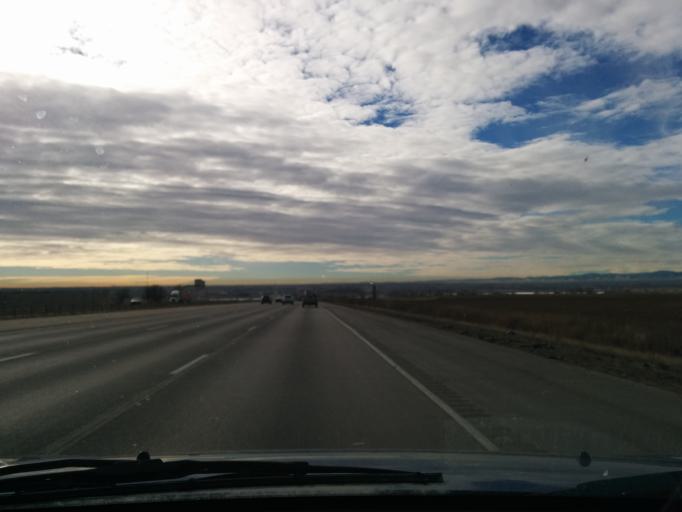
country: US
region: Colorado
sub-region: Weld County
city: Mead
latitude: 40.1882
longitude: -104.9805
